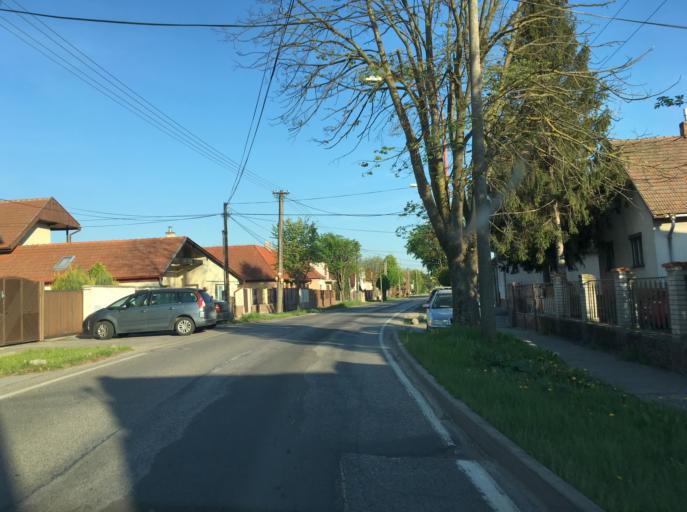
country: AT
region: Burgenland
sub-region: Politischer Bezirk Neusiedl am See
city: Deutsch Jahrndorf
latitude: 48.0569
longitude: 17.1426
